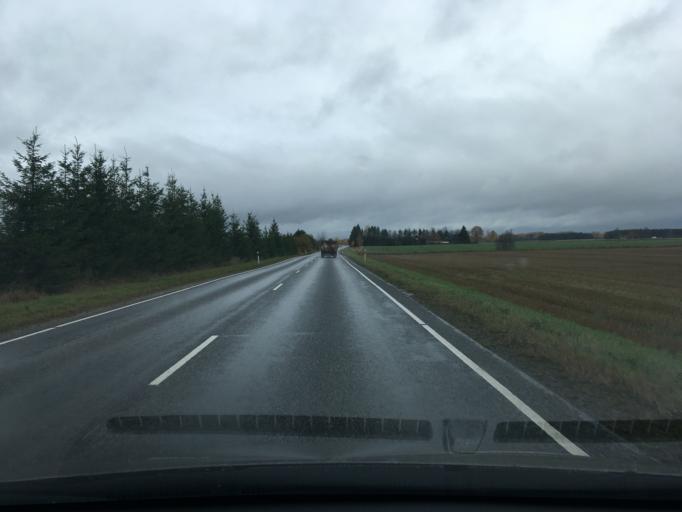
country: EE
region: Jogevamaa
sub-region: Tabivere vald
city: Tabivere
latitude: 58.4654
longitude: 26.6283
